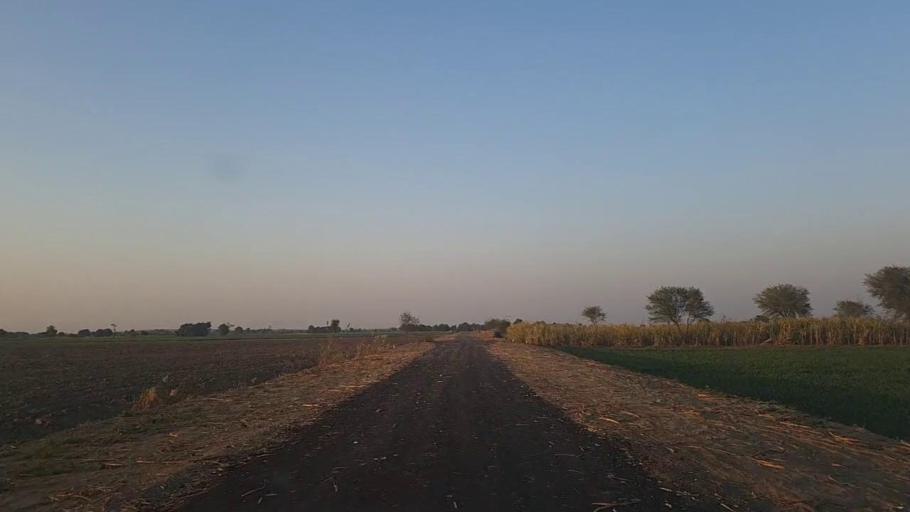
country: PK
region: Sindh
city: Jam Sahib
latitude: 26.3588
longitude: 68.7206
